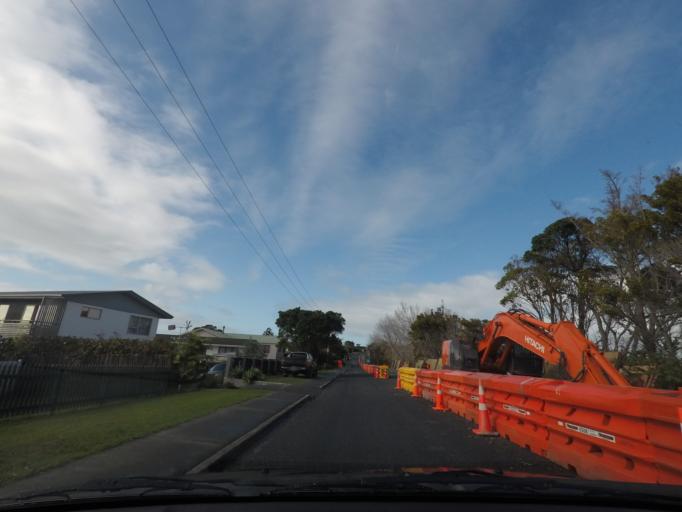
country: NZ
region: Auckland
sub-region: Auckland
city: Warkworth
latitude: -36.4345
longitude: 174.7391
